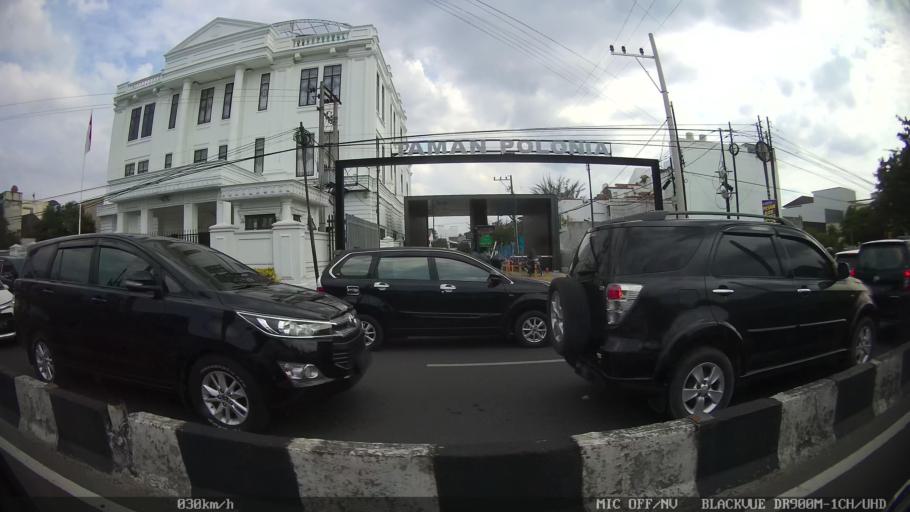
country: ID
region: North Sumatra
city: Medan
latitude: 3.5717
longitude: 98.6802
